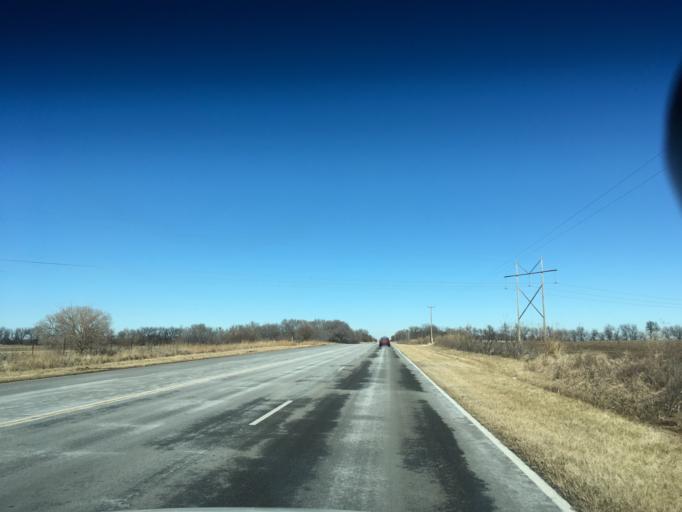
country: US
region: Kansas
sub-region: Harvey County
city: Sedgwick
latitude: 37.9157
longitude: -97.3365
